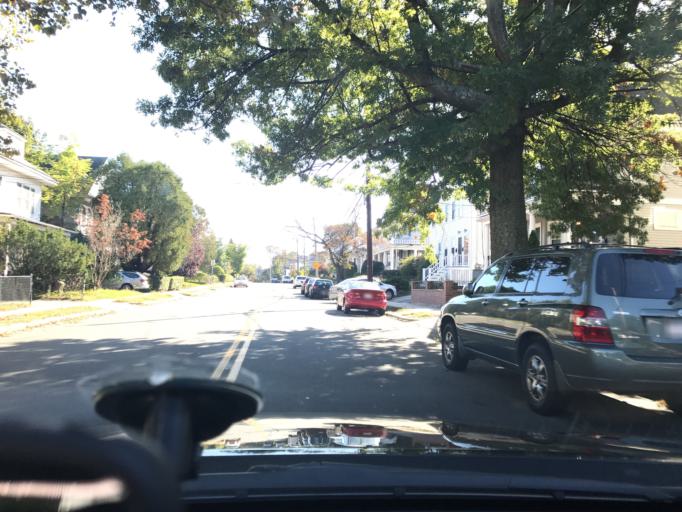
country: US
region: Massachusetts
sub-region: Middlesex County
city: Watertown
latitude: 42.3688
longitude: -71.1656
